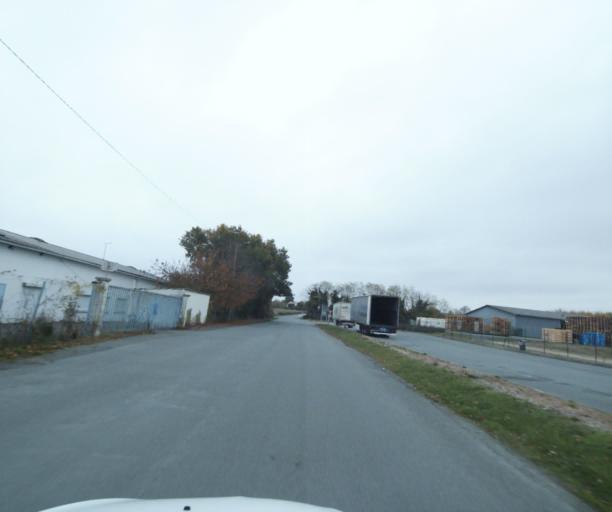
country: FR
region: Poitou-Charentes
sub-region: Departement de la Charente-Maritime
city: Les Gonds
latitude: 45.7382
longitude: -0.6105
